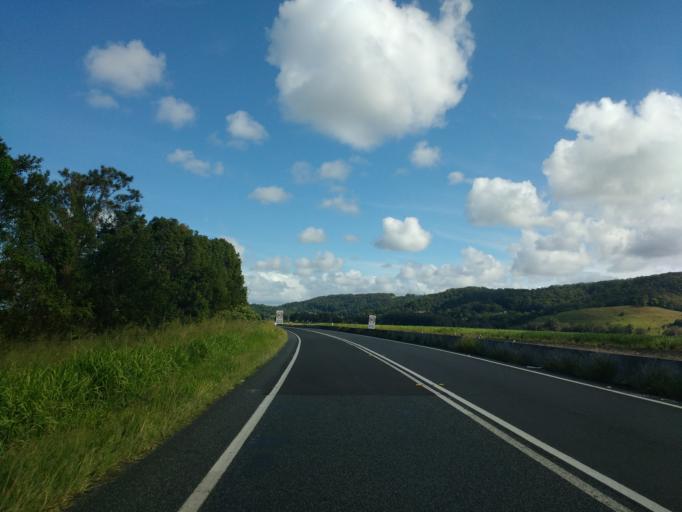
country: AU
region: New South Wales
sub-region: Ballina
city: Ballina
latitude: -28.8831
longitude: 153.4848
